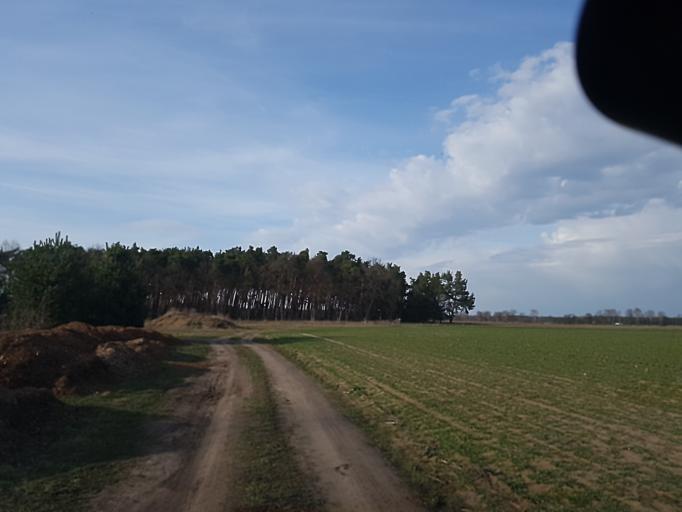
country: DE
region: Brandenburg
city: Bad Liebenwerda
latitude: 51.5495
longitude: 13.3375
